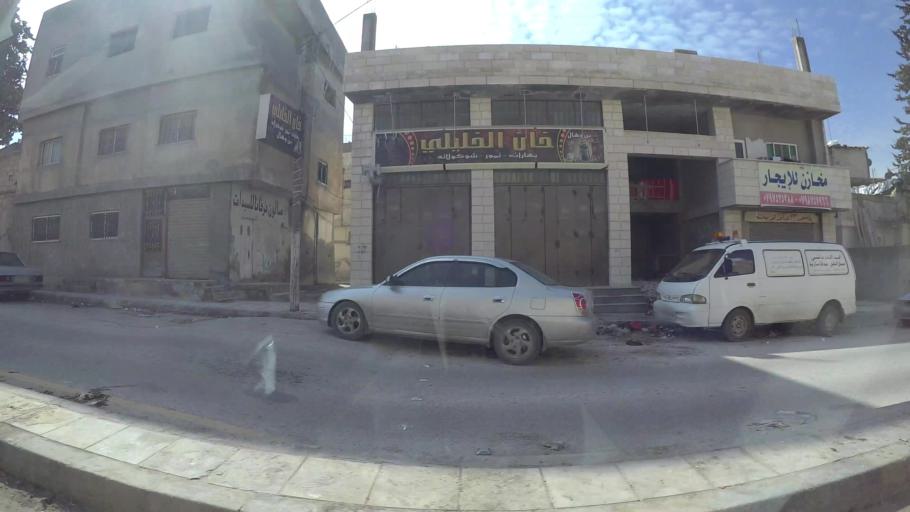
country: JO
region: Amman
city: Al Jubayhah
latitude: 32.0778
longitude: 35.8419
